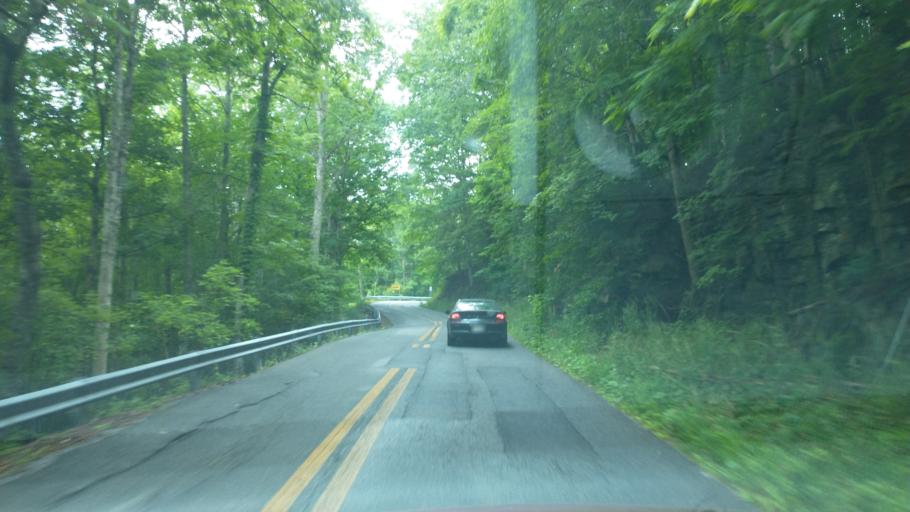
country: US
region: West Virginia
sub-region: Mercer County
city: Athens
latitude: 37.4242
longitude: -81.0034
